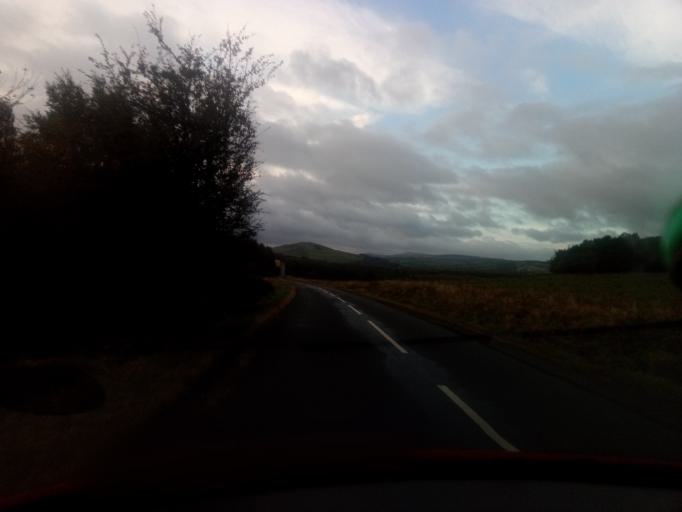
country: GB
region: Scotland
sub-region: The Scottish Borders
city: Jedburgh
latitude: 55.4325
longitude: -2.6087
